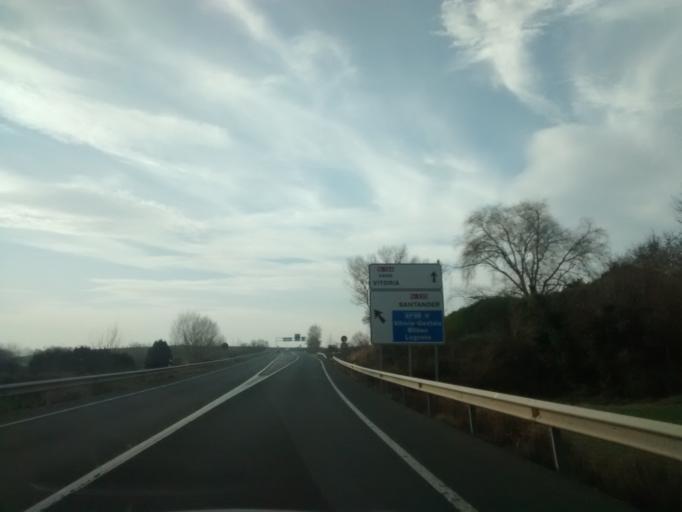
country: ES
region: La Rioja
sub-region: Provincia de La Rioja
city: Gimileo
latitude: 42.5475
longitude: -2.8258
